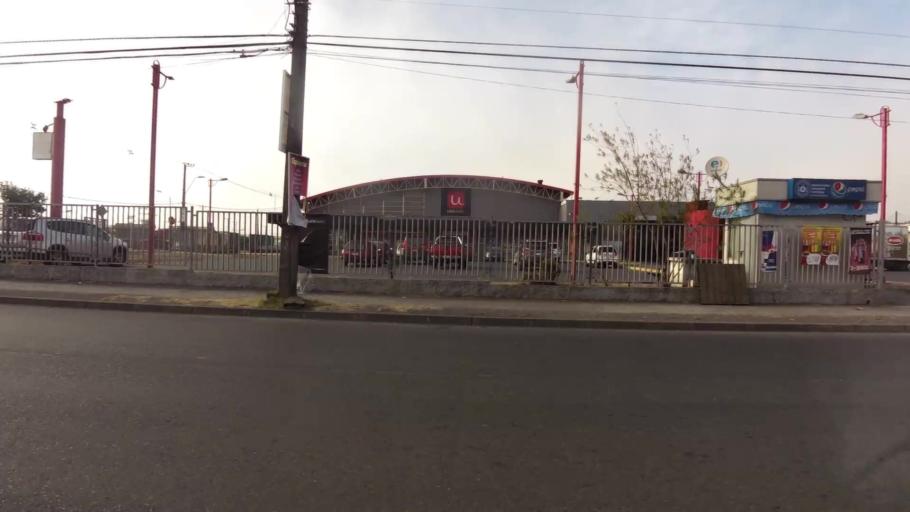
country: CL
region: Biobio
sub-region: Provincia de Concepcion
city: Concepcion
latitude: -36.7974
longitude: -73.1075
